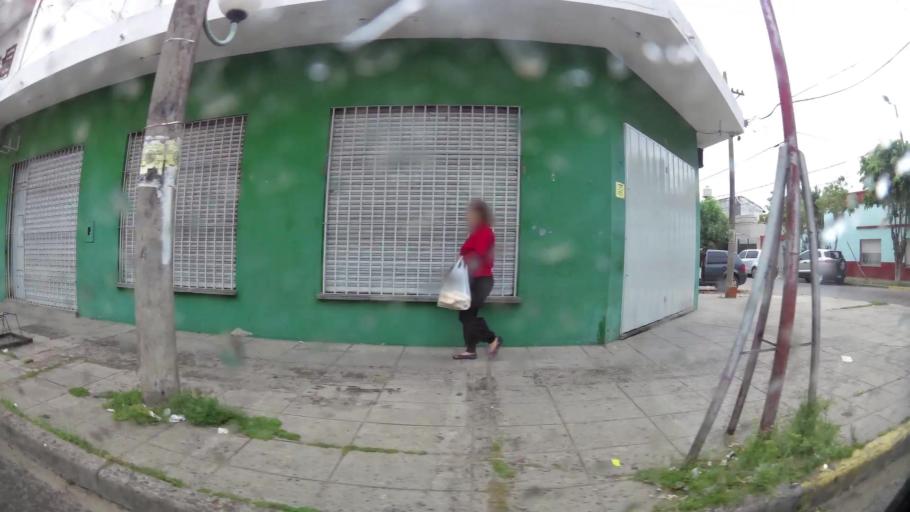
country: AR
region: Buenos Aires
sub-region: Partido de Zarate
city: Zarate
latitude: -34.0888
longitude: -59.0303
